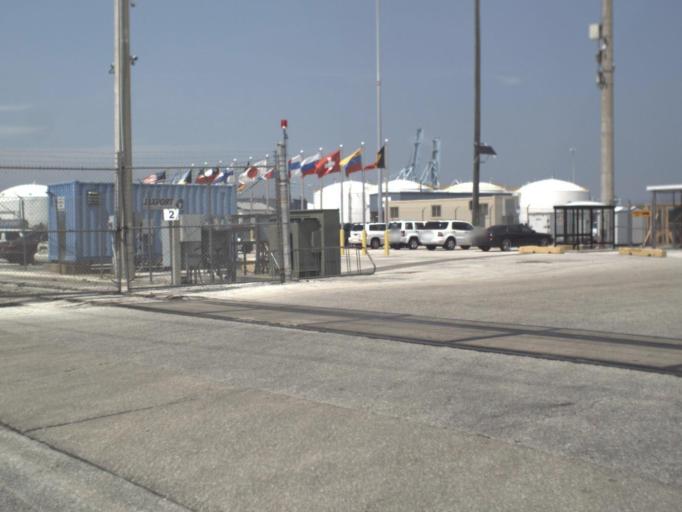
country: US
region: Florida
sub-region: Duval County
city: Jacksonville
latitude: 30.3496
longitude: -81.6259
